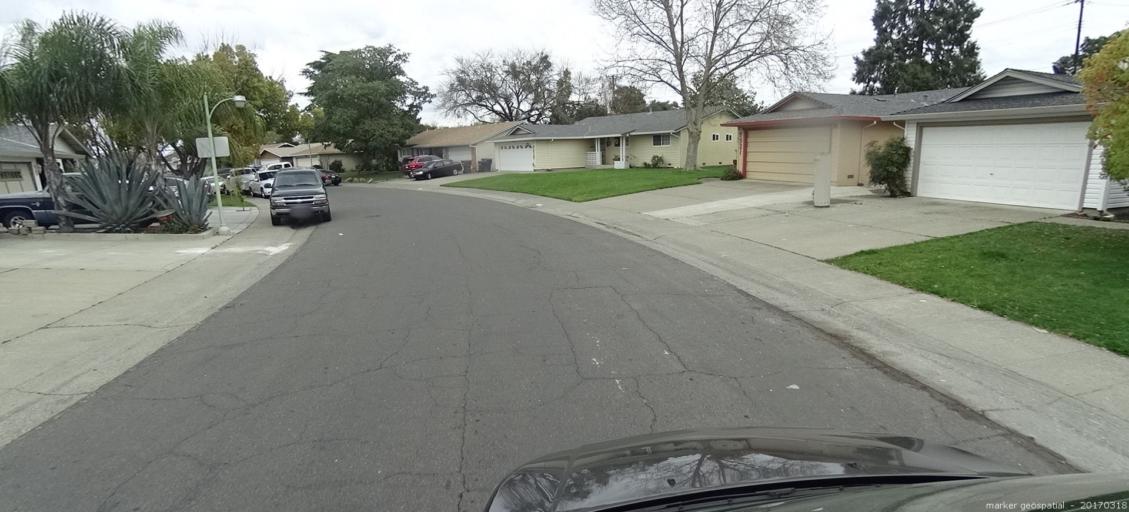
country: US
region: California
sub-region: Sacramento County
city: Parkway
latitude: 38.4841
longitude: -121.4480
